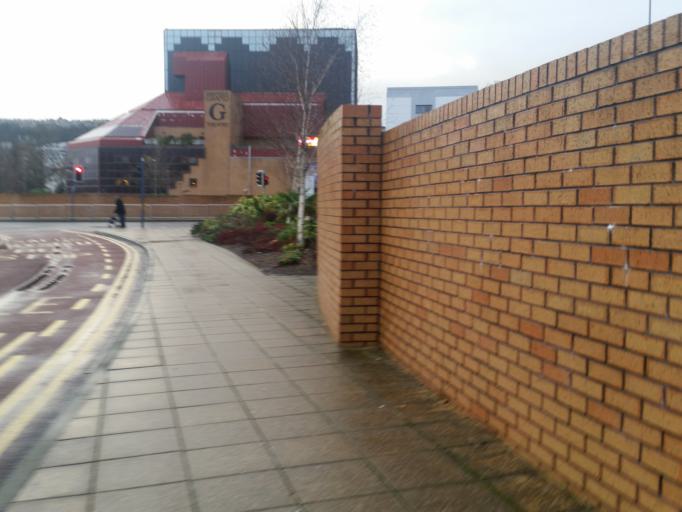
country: GB
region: Wales
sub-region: City and County of Swansea
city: Swansea
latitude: 51.6173
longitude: -3.9468
